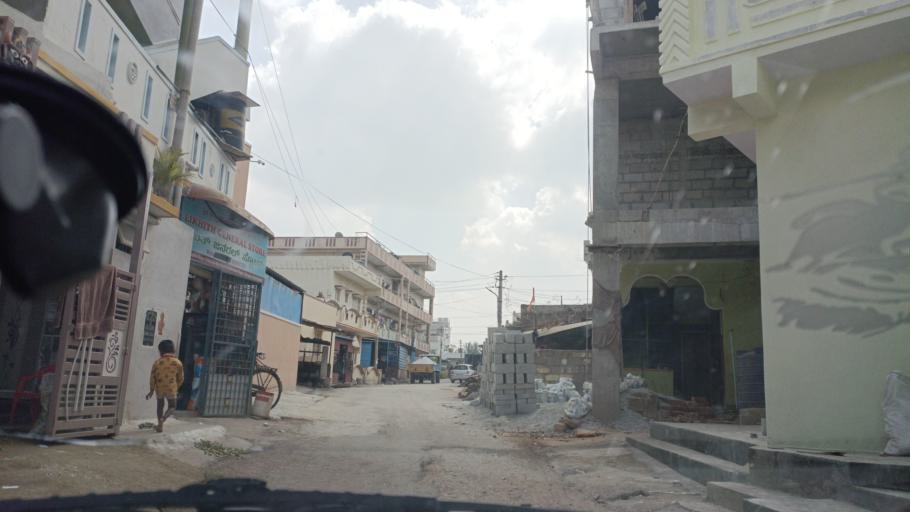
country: IN
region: Karnataka
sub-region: Bangalore Urban
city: Yelahanka
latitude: 13.1661
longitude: 77.6352
